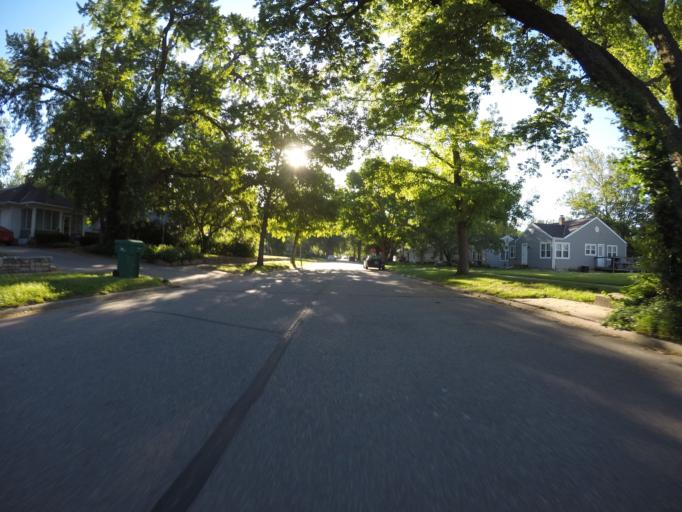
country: US
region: Kansas
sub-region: Riley County
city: Manhattan
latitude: 39.1920
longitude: -96.5723
